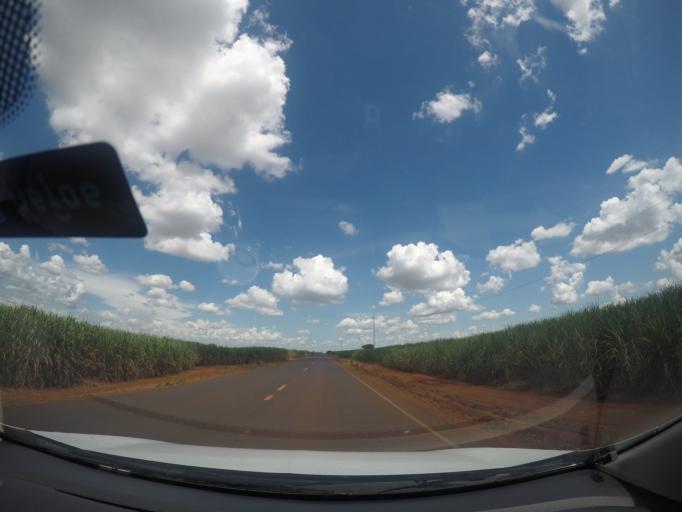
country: BR
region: Minas Gerais
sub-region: Frutal
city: Frutal
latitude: -19.8549
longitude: -48.7344
